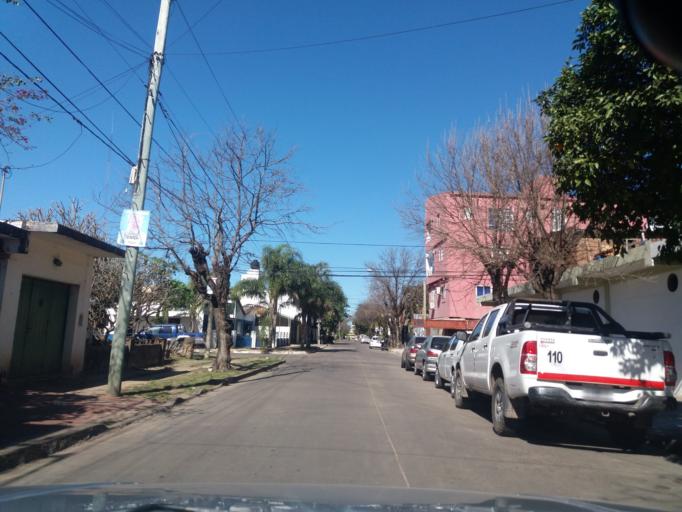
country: AR
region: Corrientes
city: Corrientes
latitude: -27.4746
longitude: -58.8198
